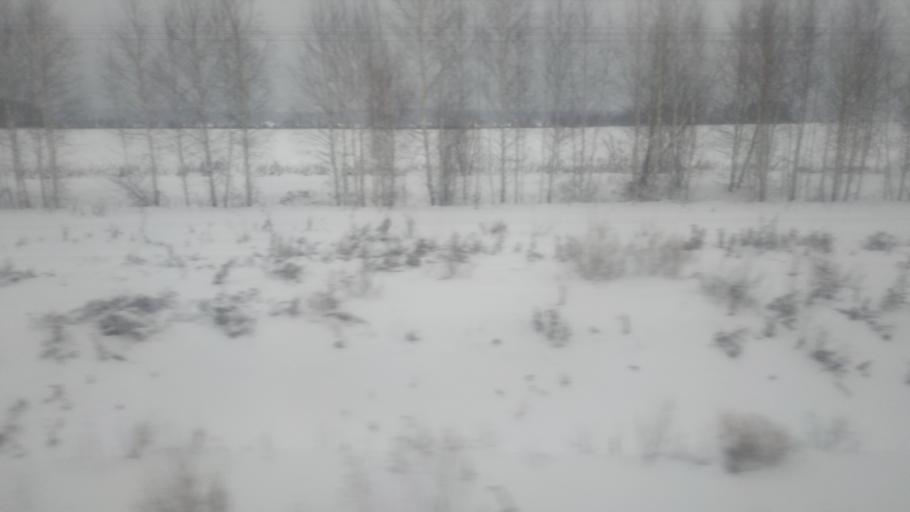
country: RU
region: Bashkortostan
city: Amzya
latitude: 56.2481
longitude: 54.6449
